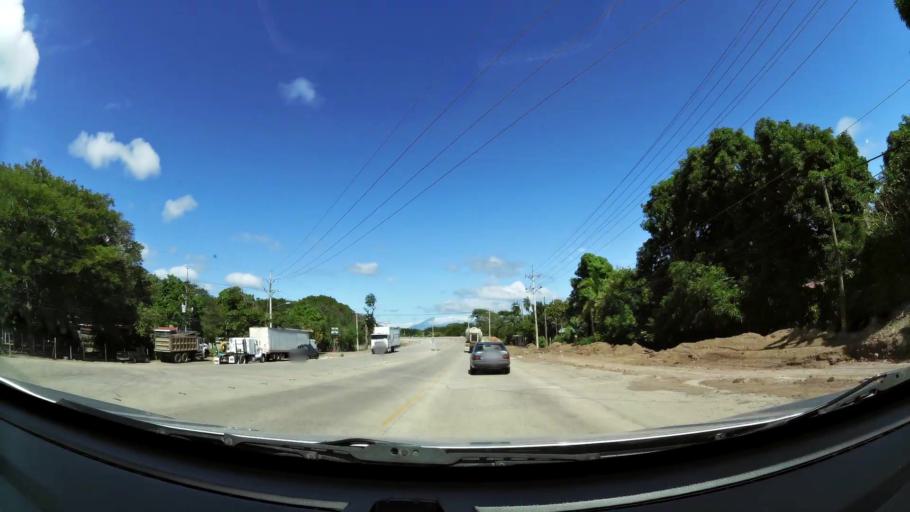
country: CR
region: Guanacaste
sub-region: Canton de Canas
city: Canas
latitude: 10.4181
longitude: -85.0873
